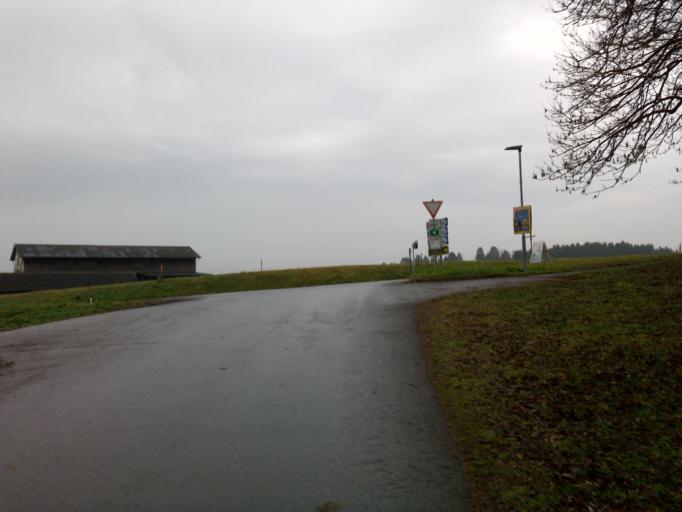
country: AT
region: Styria
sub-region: Politischer Bezirk Murtal
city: Sankt Marein bei Knittelfeld
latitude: 47.2817
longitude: 14.8709
